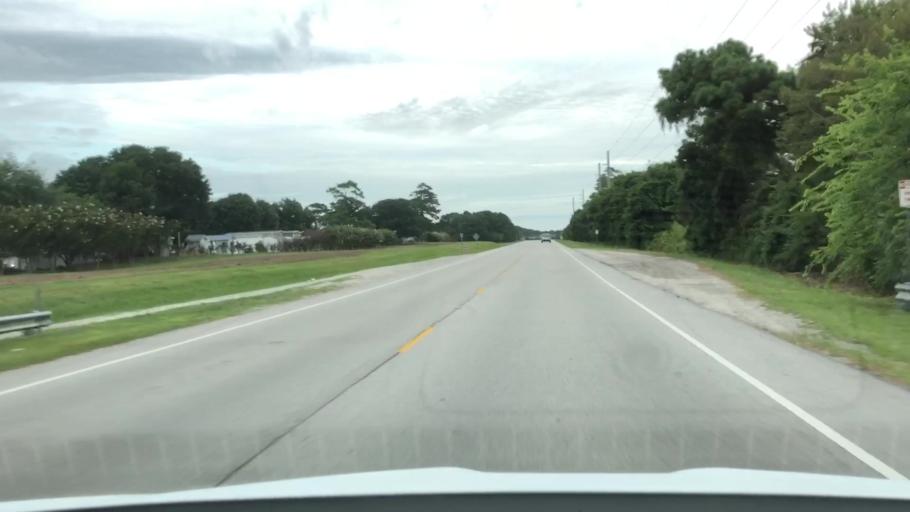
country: US
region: North Carolina
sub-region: Carteret County
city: Cedar Point
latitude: 34.6803
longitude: -77.0673
